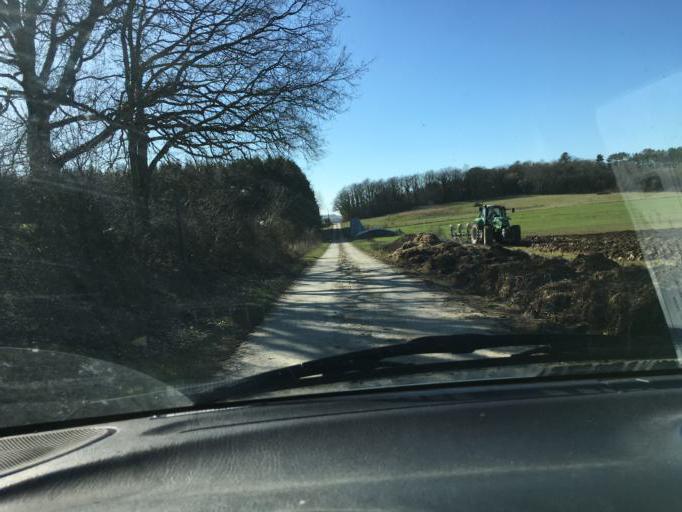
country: BE
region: Wallonia
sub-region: Province de Namur
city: Doische
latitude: 50.1211
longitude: 4.6749
